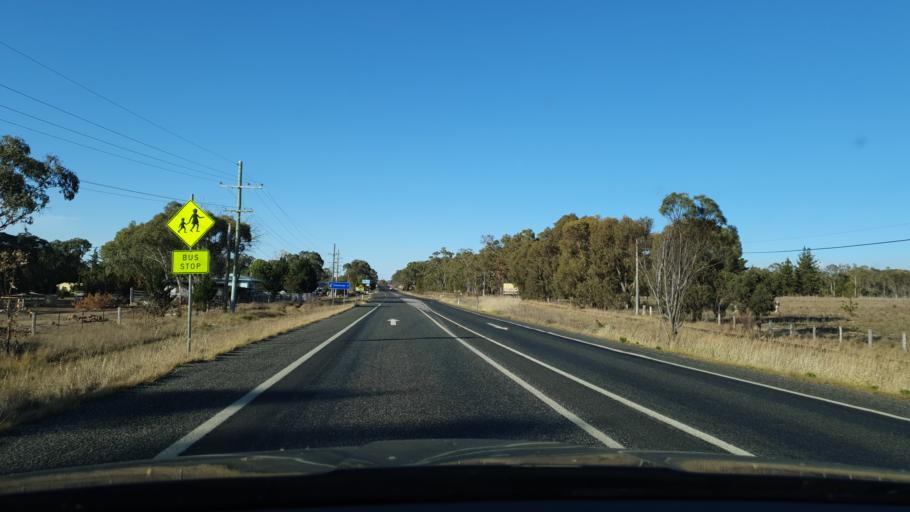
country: AU
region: Queensland
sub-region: Southern Downs
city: Stanthorpe
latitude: -28.6995
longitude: 151.9055
